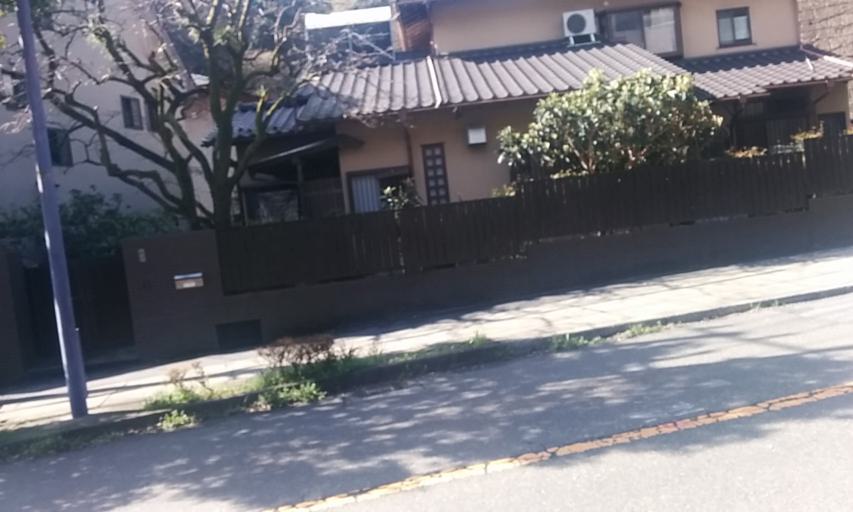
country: JP
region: Kanagawa
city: Kamakura
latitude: 35.3209
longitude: 139.5412
